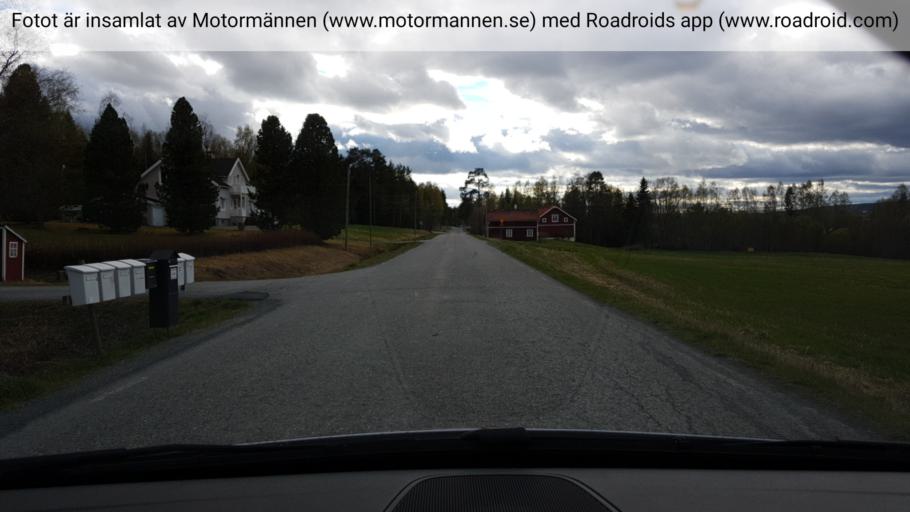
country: SE
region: Jaemtland
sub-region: OEstersunds Kommun
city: Lit
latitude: 63.3082
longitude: 14.8765
